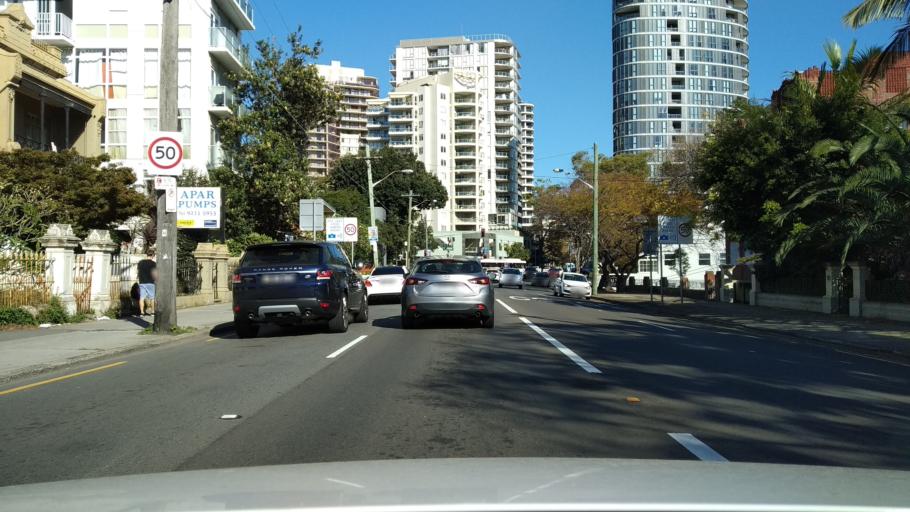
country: AU
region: New South Wales
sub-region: Waverley
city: Bondi Junction
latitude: -33.8904
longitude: 151.2544
